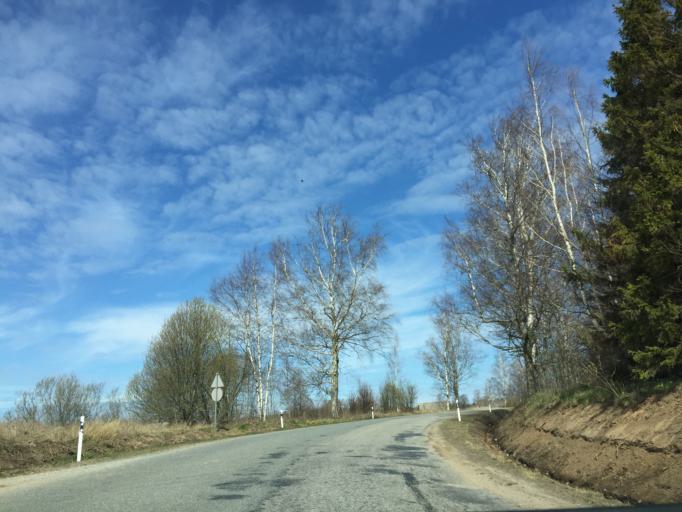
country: LV
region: Salacgrivas
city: Salacgriva
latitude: 57.7512
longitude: 24.4014
